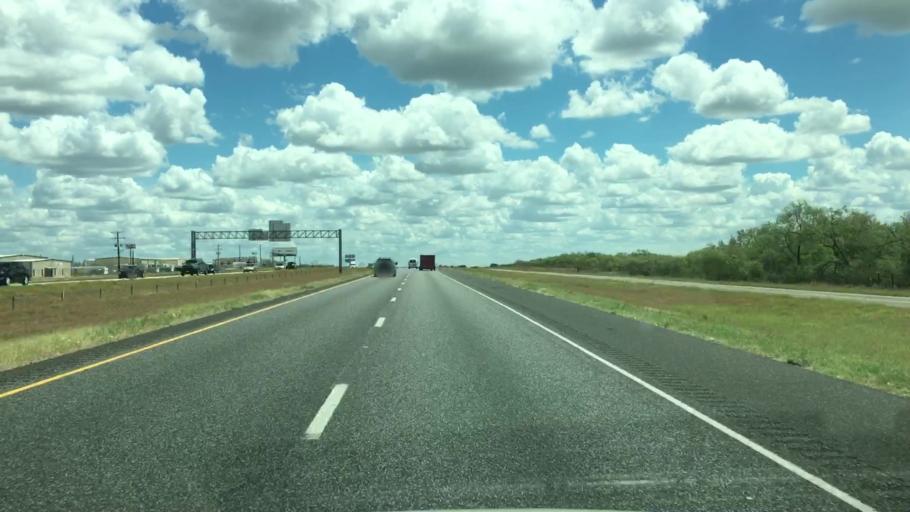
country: US
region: Texas
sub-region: Atascosa County
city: Pleasanton
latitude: 28.8932
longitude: -98.4125
